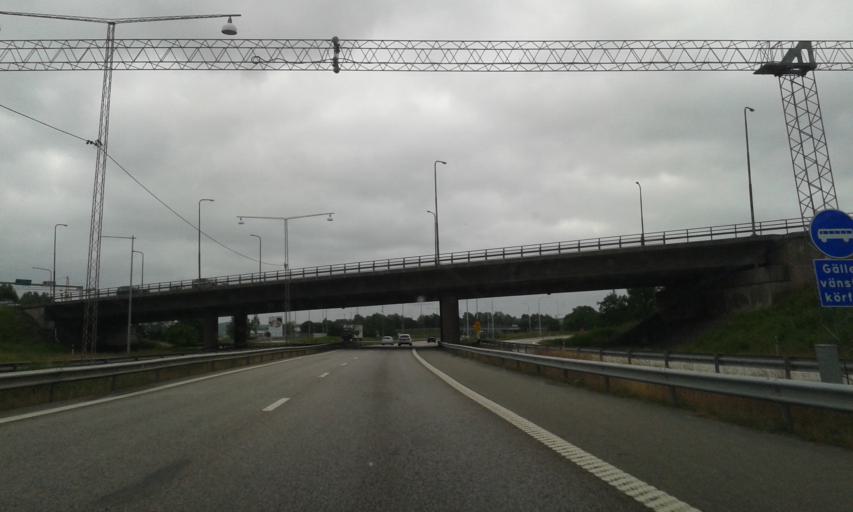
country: SE
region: Vaestra Goetaland
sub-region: Kungalvs Kommun
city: Kungalv
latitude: 57.8759
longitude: 11.9626
